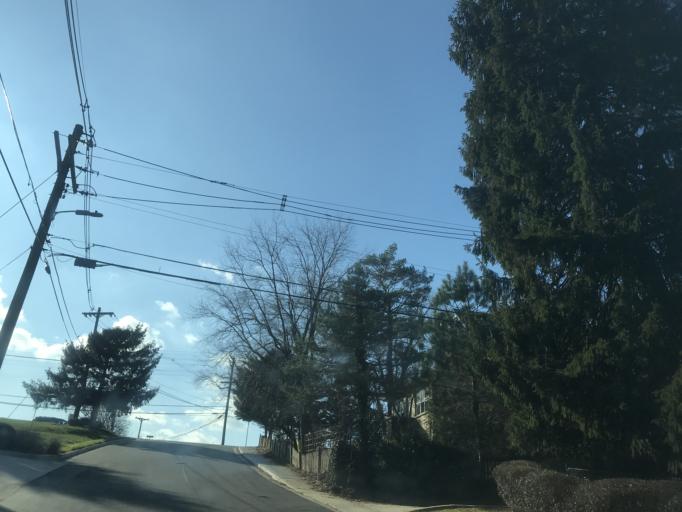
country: US
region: Maryland
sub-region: Baltimore County
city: Towson
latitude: 39.3984
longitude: -76.5820
